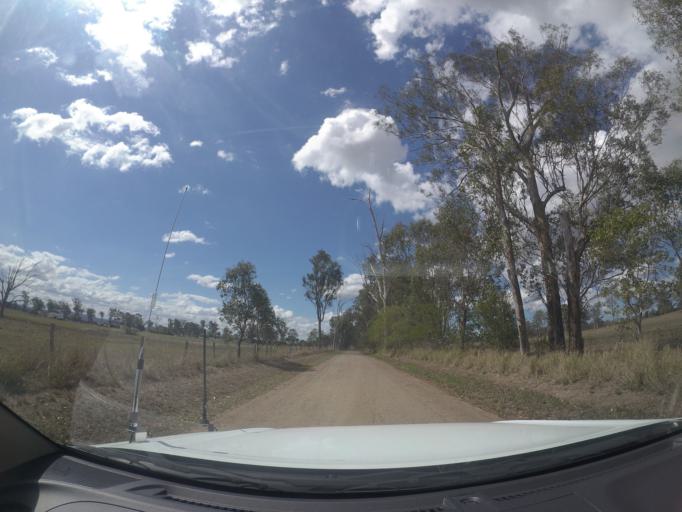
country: AU
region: Queensland
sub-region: Logan
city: Cedar Vale
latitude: -27.8884
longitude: 152.9599
